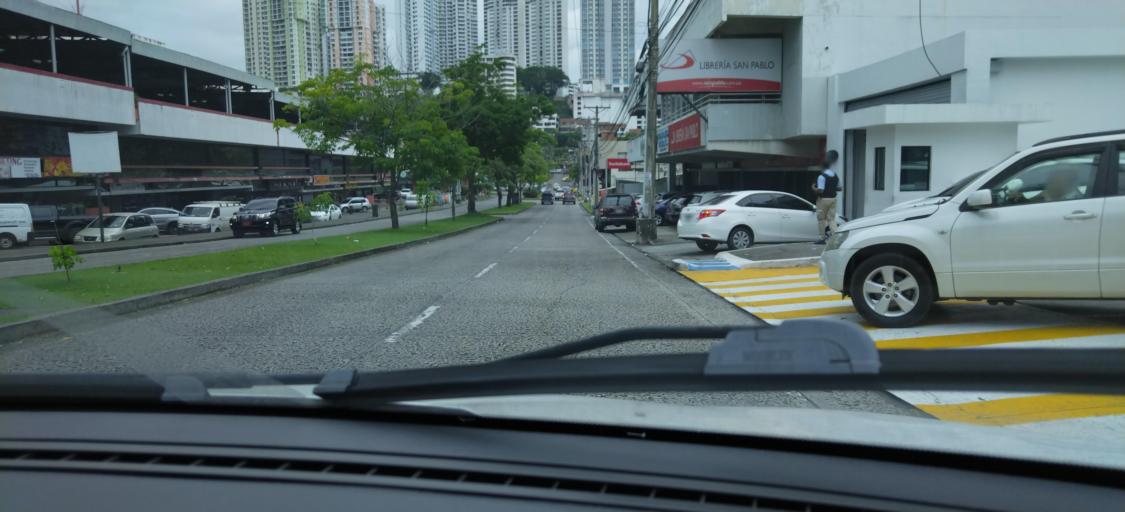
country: PA
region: Panama
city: Panama
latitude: 9.0086
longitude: -79.5367
